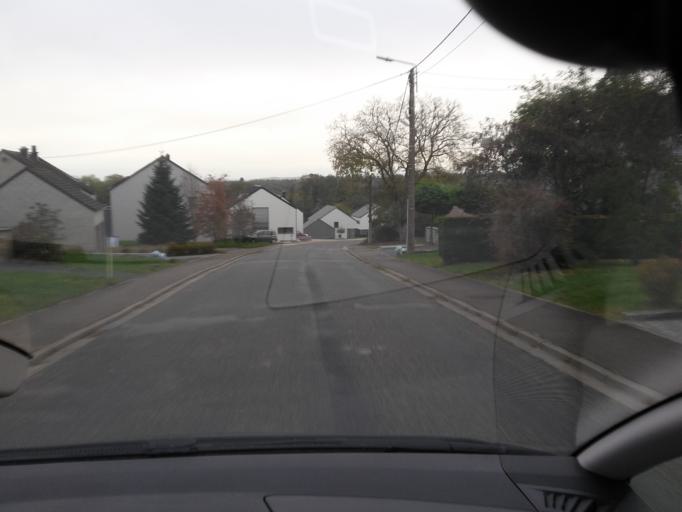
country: BE
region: Wallonia
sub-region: Province du Luxembourg
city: Attert
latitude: 49.7024
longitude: 5.7447
